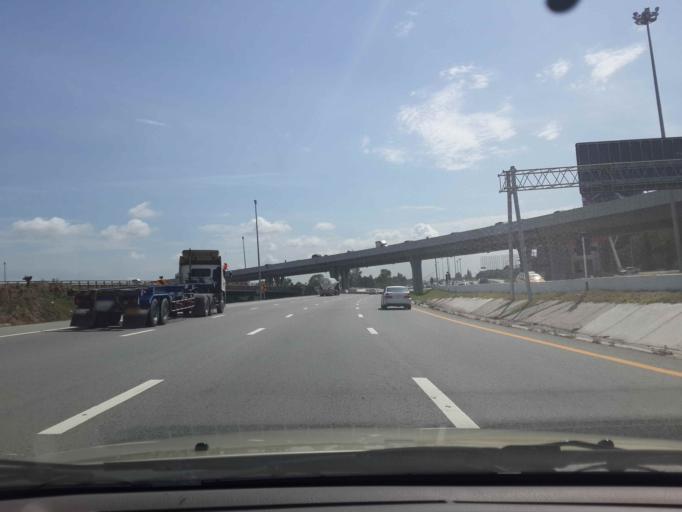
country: TH
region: Chon Buri
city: Chon Buri
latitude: 13.2992
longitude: 100.9950
